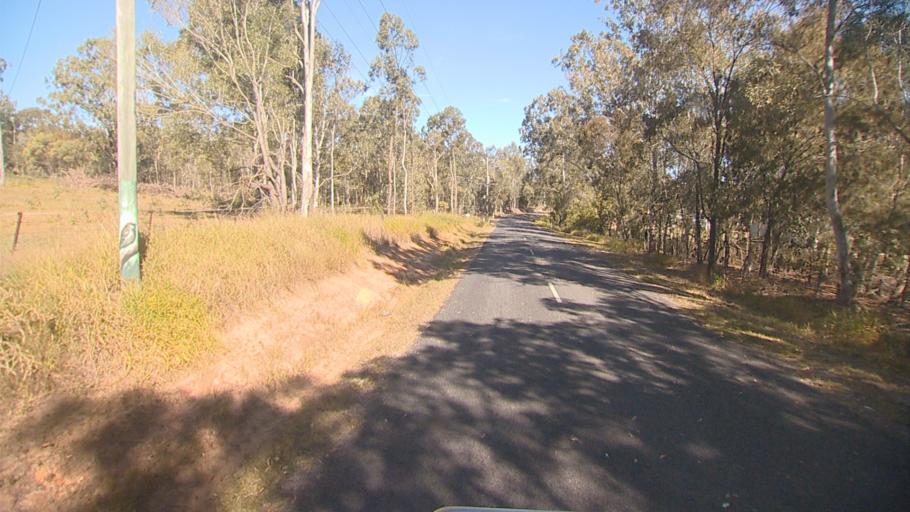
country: AU
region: Queensland
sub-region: Ipswich
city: Springfield Lakes
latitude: -27.7162
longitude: 152.9400
